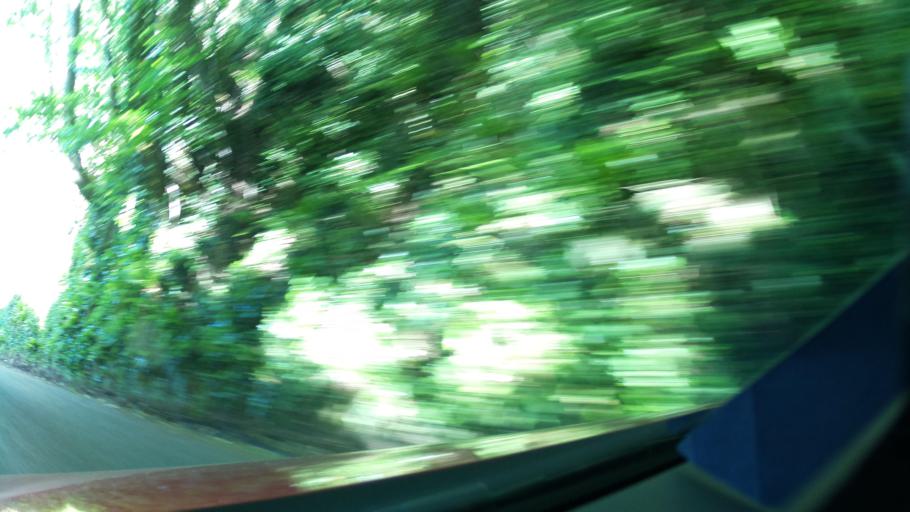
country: GB
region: England
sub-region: Somerset
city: Yeovil
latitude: 50.9392
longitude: -2.6018
